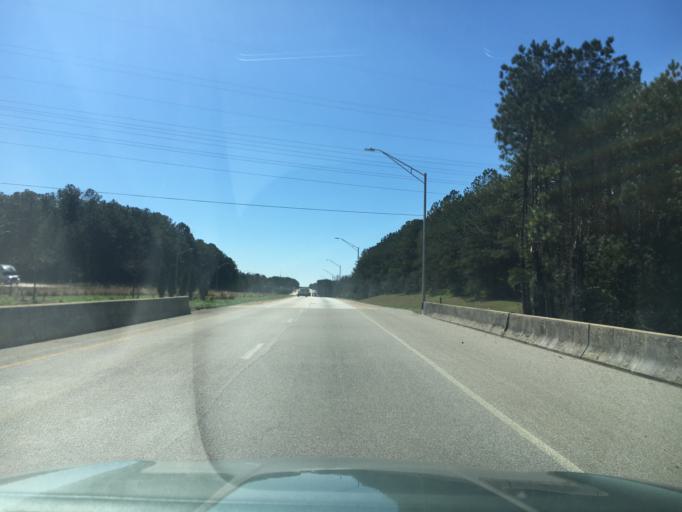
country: US
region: Georgia
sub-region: Troup County
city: La Grange
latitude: 33.0421
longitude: -84.9700
